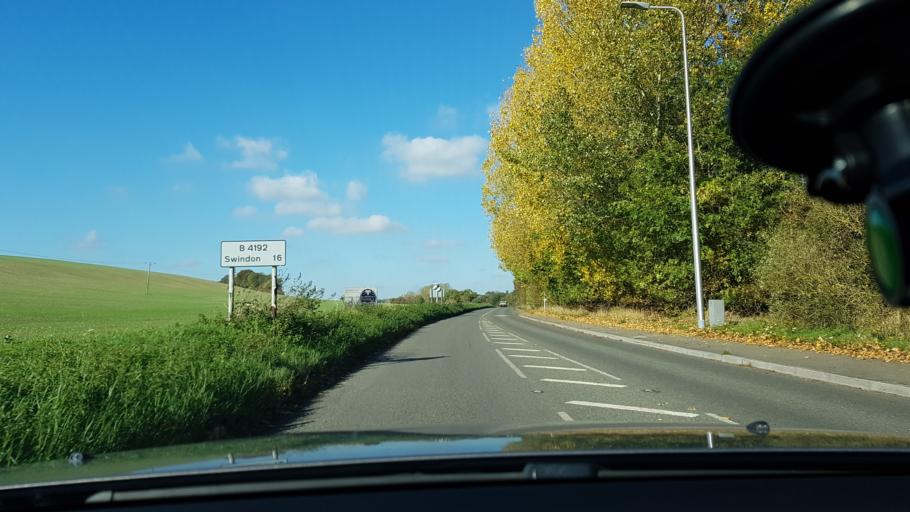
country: GB
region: England
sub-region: West Berkshire
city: Hungerford
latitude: 51.4202
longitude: -1.5195
